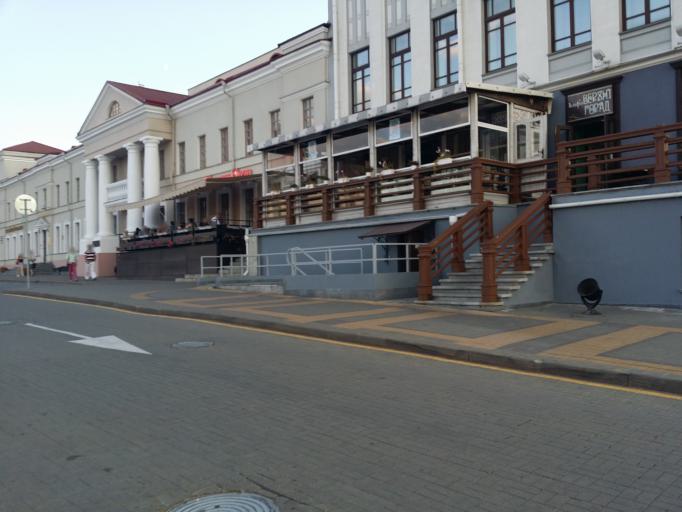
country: BY
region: Minsk
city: Minsk
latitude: 53.9046
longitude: 27.5559
